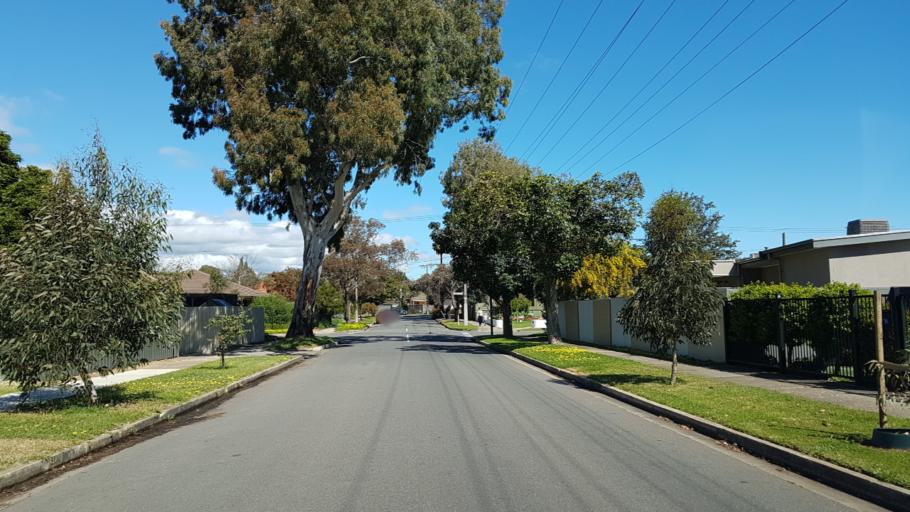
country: AU
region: South Australia
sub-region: Marion
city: Plympton Park
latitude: -34.9957
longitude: 138.5517
